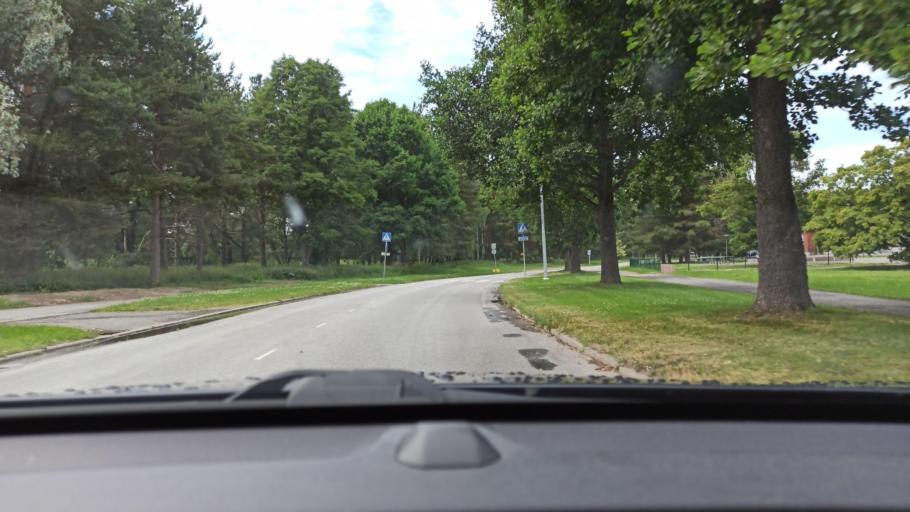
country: FI
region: Satakunta
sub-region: Pori
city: Pori
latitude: 61.4975
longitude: 21.7880
